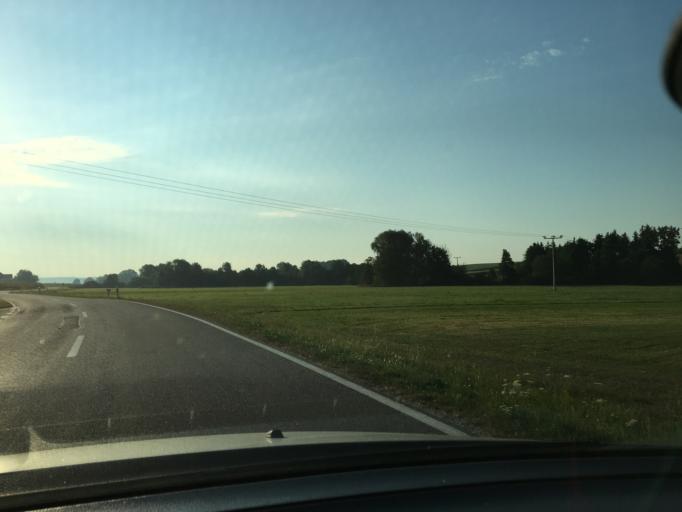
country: DE
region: Bavaria
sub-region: Lower Bavaria
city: Schalkham
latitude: 48.4980
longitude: 12.3747
